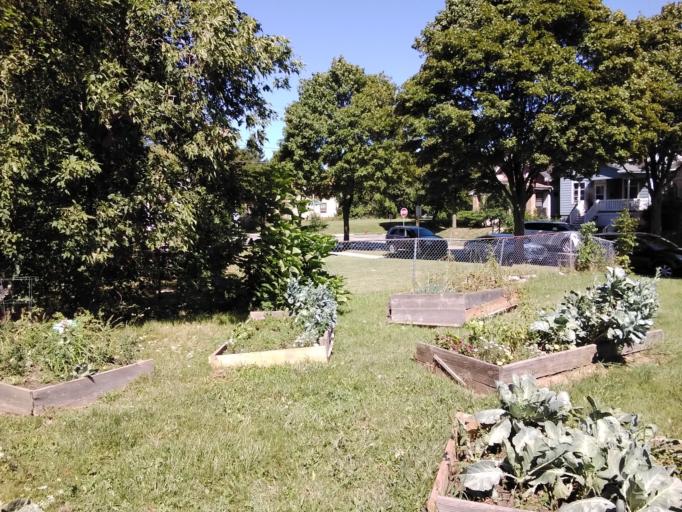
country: US
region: Wisconsin
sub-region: Milwaukee County
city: Milwaukee
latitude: 43.0728
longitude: -87.9371
